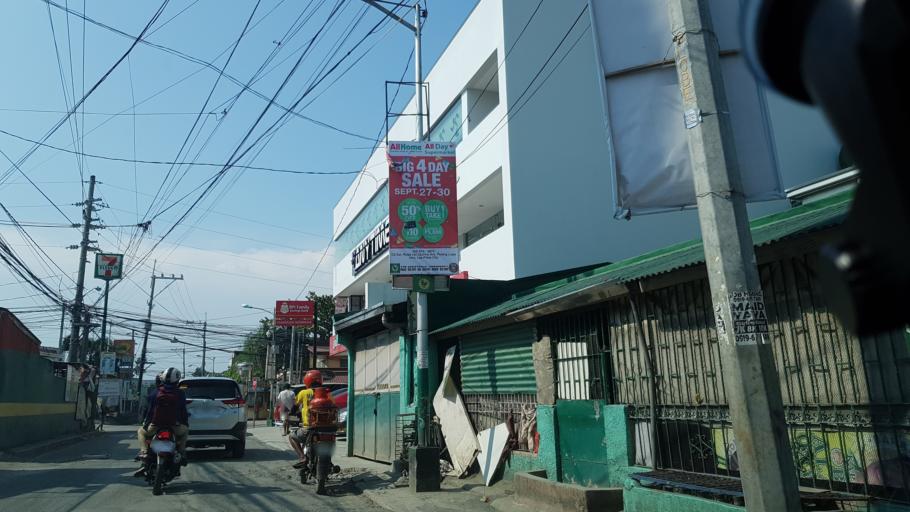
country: PH
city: Sambayanihan People's Village
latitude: 14.4972
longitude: 121.0133
